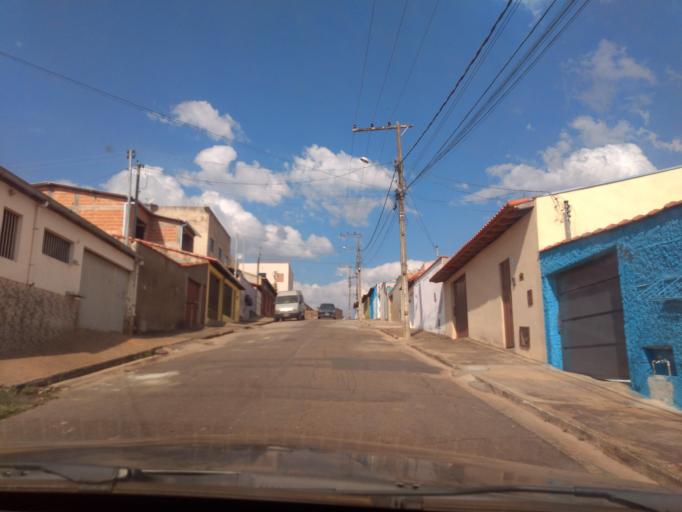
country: BR
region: Minas Gerais
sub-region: Tres Coracoes
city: Tres Coracoes
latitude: -21.6855
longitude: -45.2358
